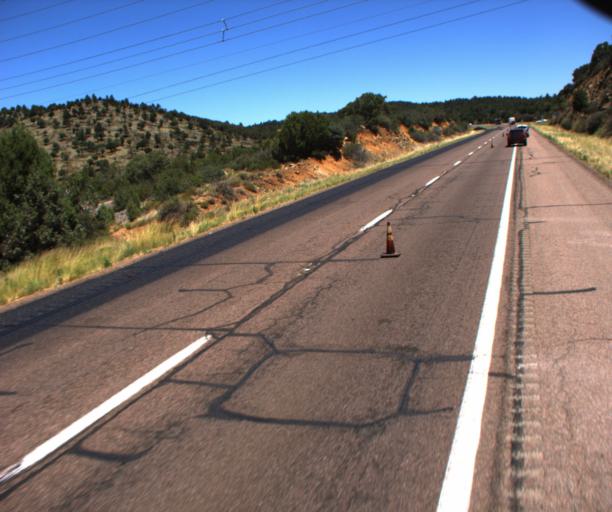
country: US
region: Arizona
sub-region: Gila County
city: Payson
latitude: 34.1903
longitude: -111.3304
